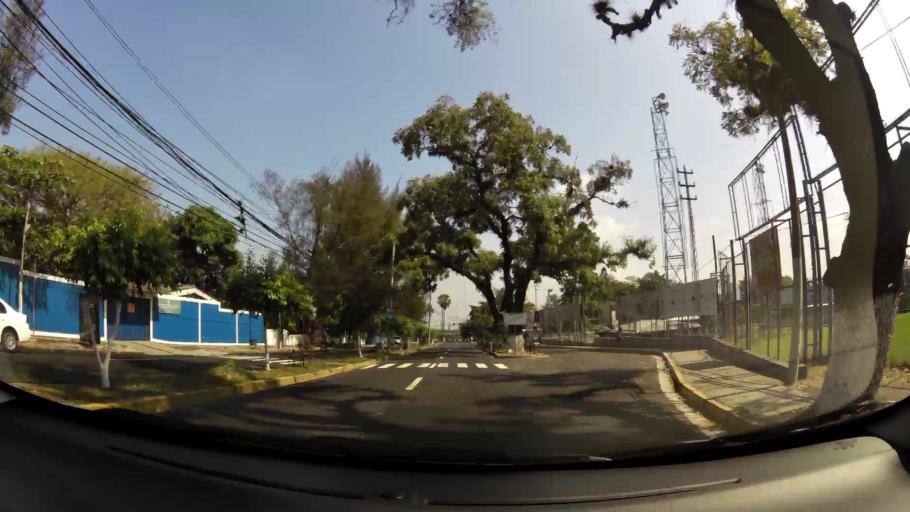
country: SV
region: La Libertad
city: Antiguo Cuscatlan
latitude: 13.6893
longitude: -89.2329
